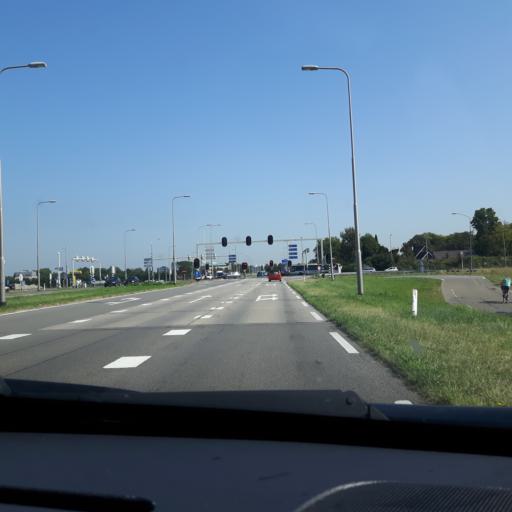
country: NL
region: Zeeland
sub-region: Gemeente Goes
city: Goes
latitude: 51.5052
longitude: 3.8691
